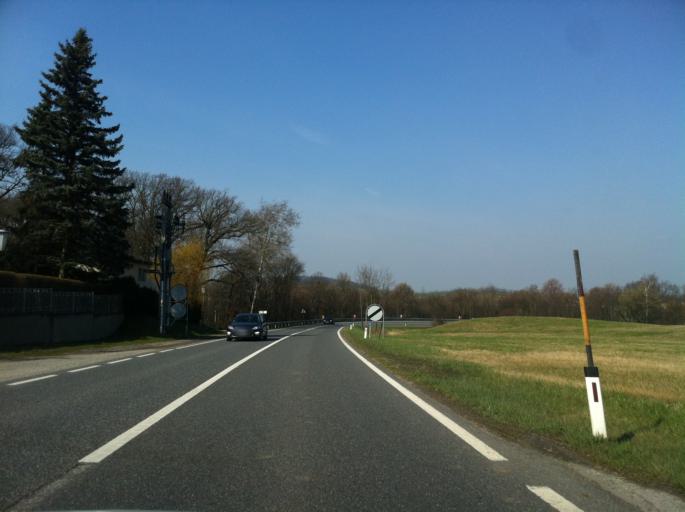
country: AT
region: Lower Austria
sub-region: Politischer Bezirk Tulln
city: Tulbing
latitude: 48.2562
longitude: 16.0847
